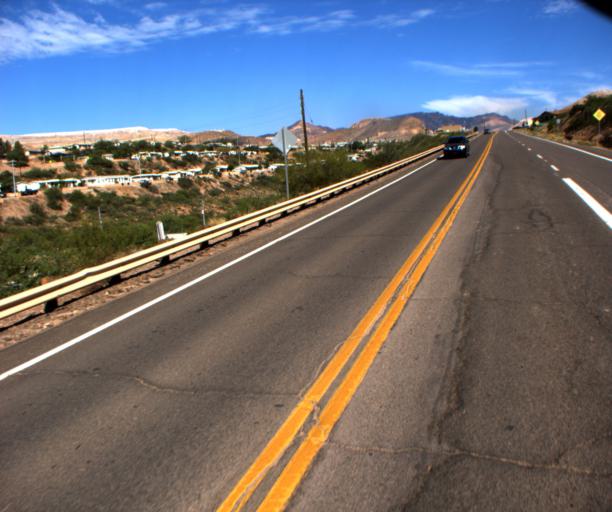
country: US
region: Arizona
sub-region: Greenlee County
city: Clifton
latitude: 33.0525
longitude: -109.3254
